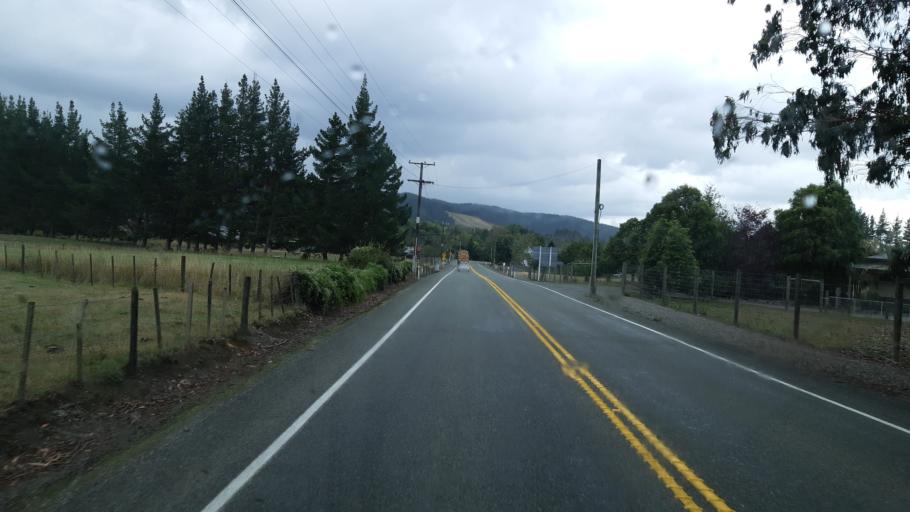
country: NZ
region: Tasman
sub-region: Tasman District
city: Wakefield
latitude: -41.4540
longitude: 172.9569
